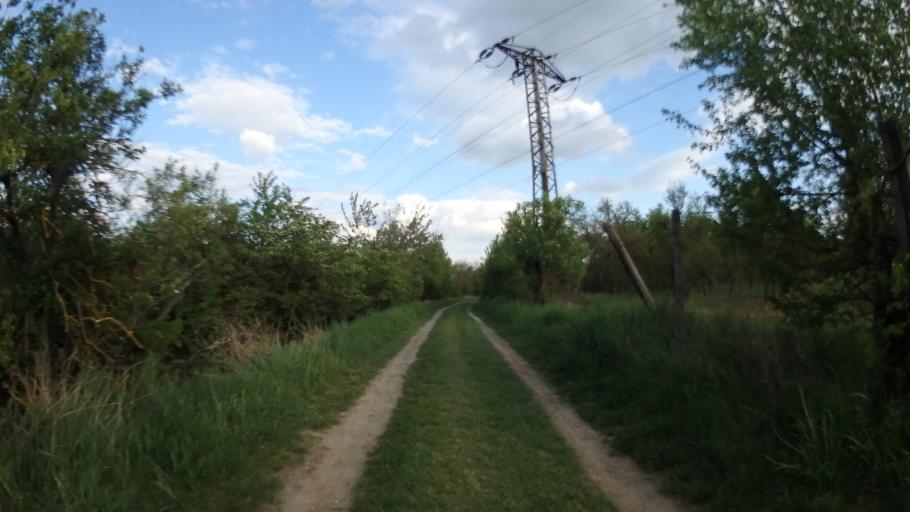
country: CZ
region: South Moravian
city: Moravany
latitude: 49.1594
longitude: 16.5738
